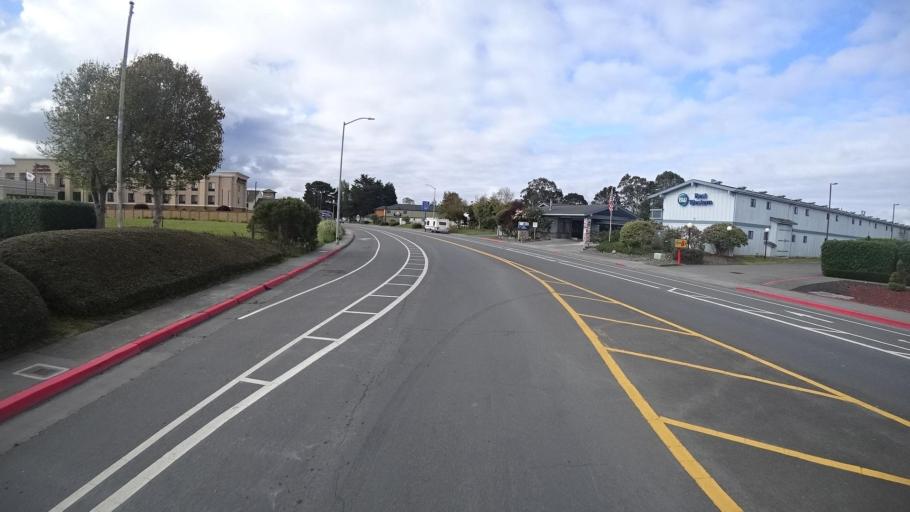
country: US
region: California
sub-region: Humboldt County
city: Arcata
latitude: 40.9024
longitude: -124.0835
